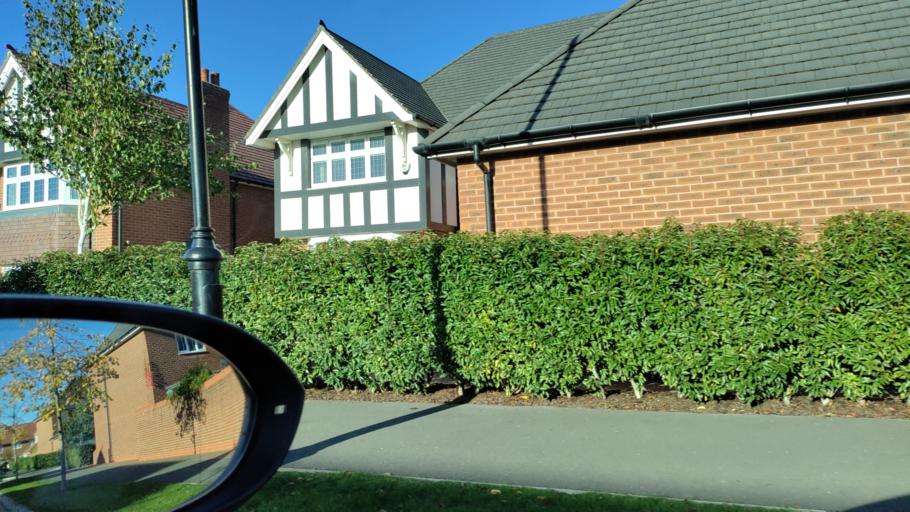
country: GB
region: England
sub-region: Cheshire West and Chester
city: Hartford
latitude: 53.2463
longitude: -2.5511
